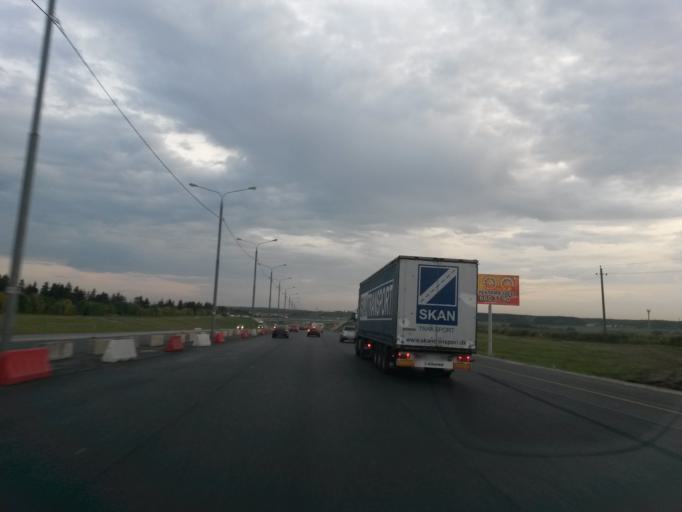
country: RU
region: Moskovskaya
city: Klimovsk
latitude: 55.3558
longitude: 37.5958
